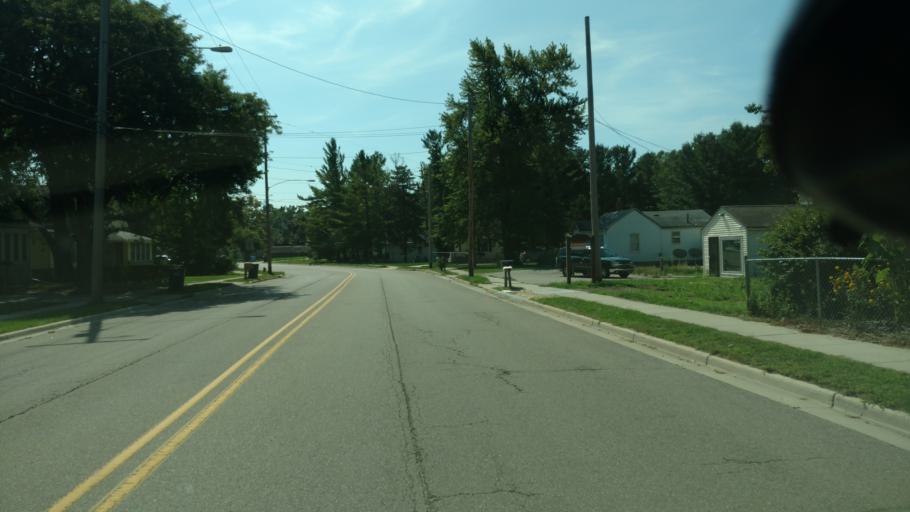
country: US
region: Michigan
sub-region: Ingham County
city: Lansing
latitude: 42.7634
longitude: -84.5557
